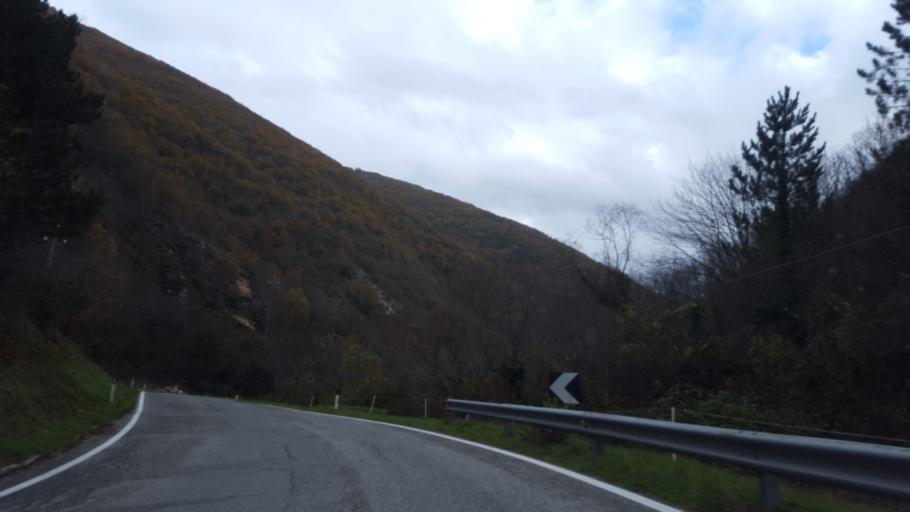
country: IT
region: The Marches
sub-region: Provincia di Macerata
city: Fluminata
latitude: 42.9144
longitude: 13.1249
